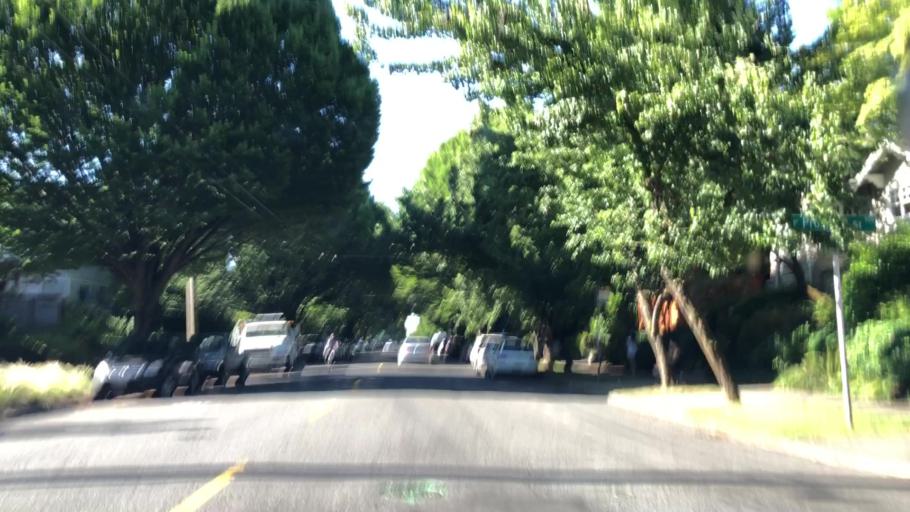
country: US
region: Washington
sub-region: King County
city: Seattle
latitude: 47.6289
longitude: -122.3073
